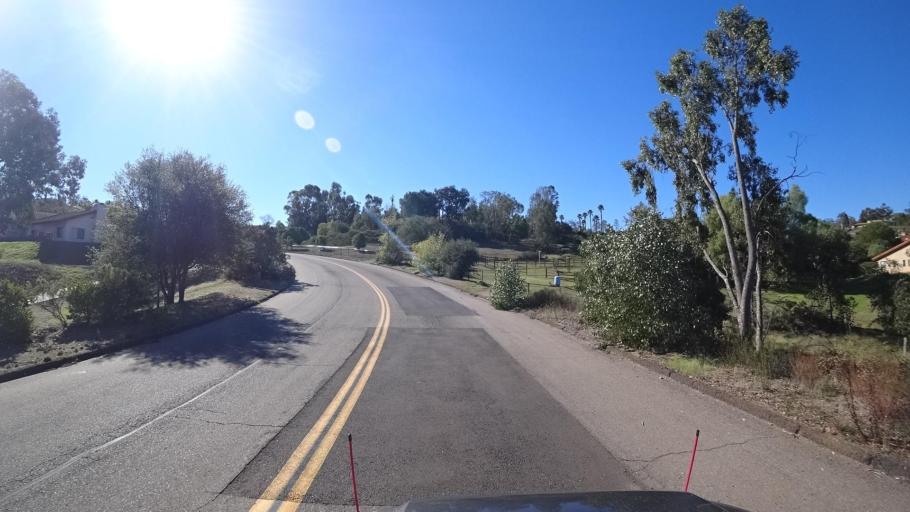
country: US
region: California
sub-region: San Diego County
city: Jamul
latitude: 32.7181
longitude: -116.8499
